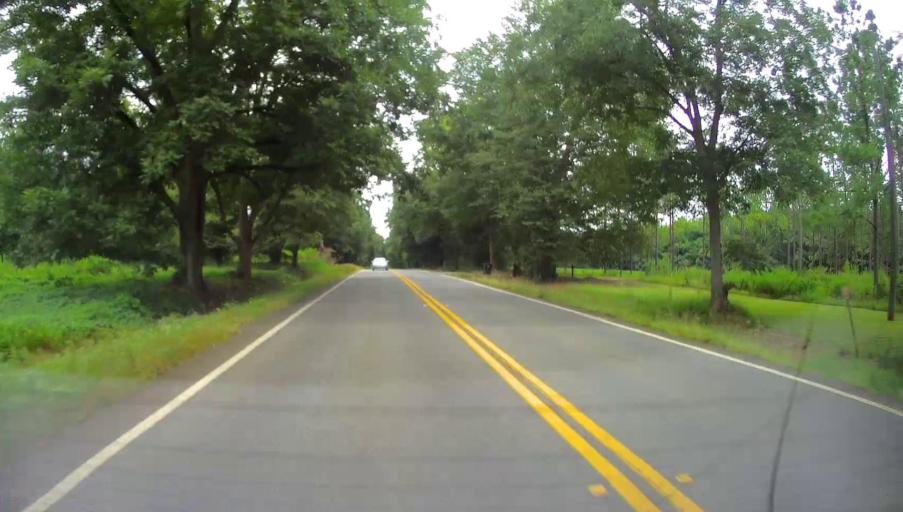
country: US
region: Georgia
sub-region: Schley County
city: Ellaville
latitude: 32.2586
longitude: -84.4173
